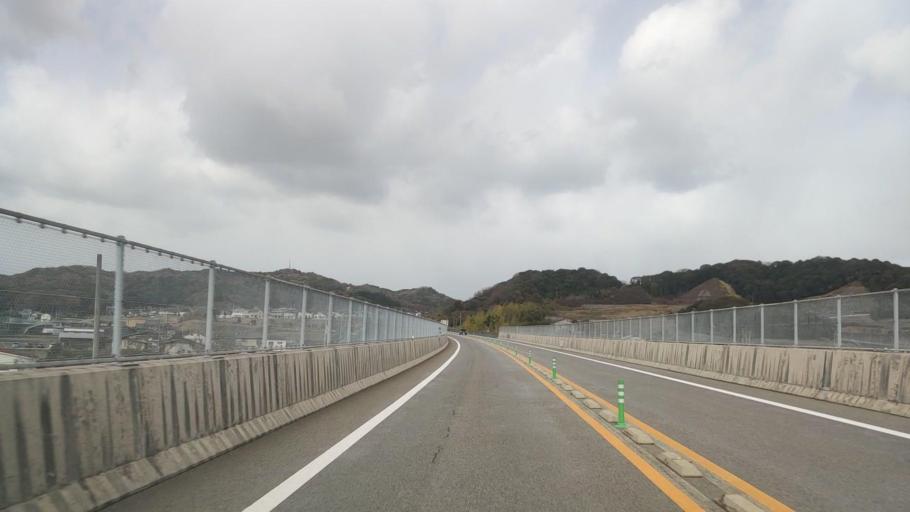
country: JP
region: Ehime
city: Hojo
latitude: 34.0620
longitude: 132.9728
